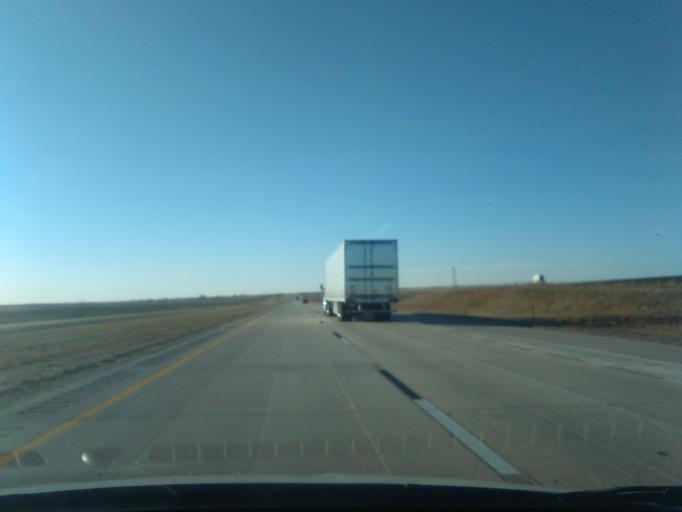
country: US
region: Nebraska
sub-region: Cheyenne County
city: Sidney
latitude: 41.1132
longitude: -102.7716
